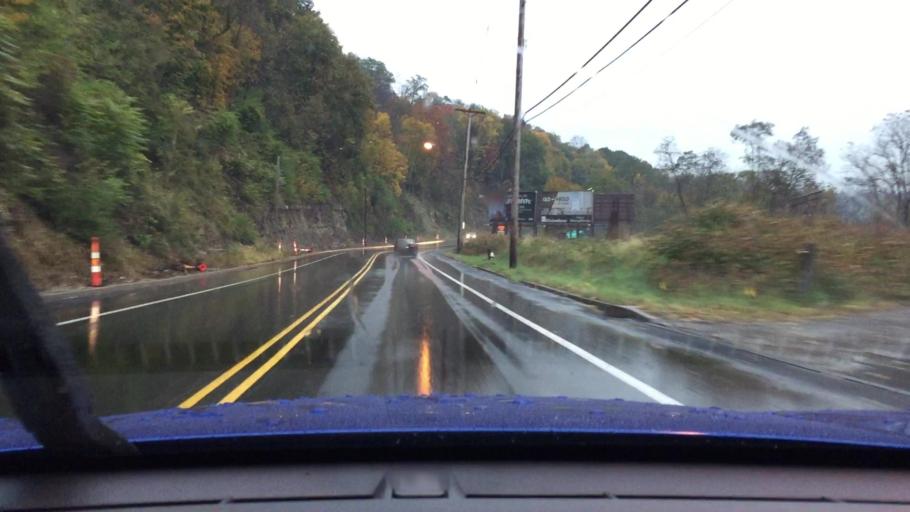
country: US
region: Pennsylvania
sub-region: Allegheny County
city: Crafton
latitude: 40.4382
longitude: -80.0474
